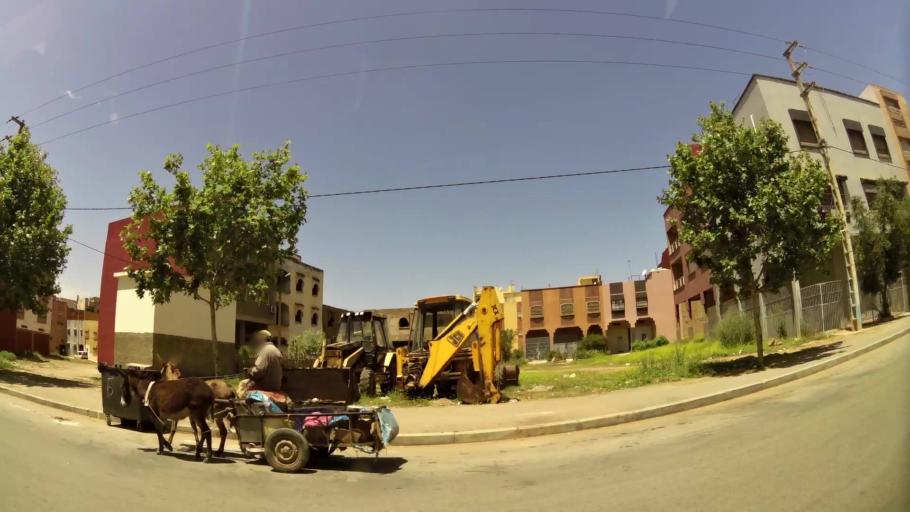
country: MA
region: Rabat-Sale-Zemmour-Zaer
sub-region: Khemisset
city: Khemisset
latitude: 33.8318
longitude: -6.0778
